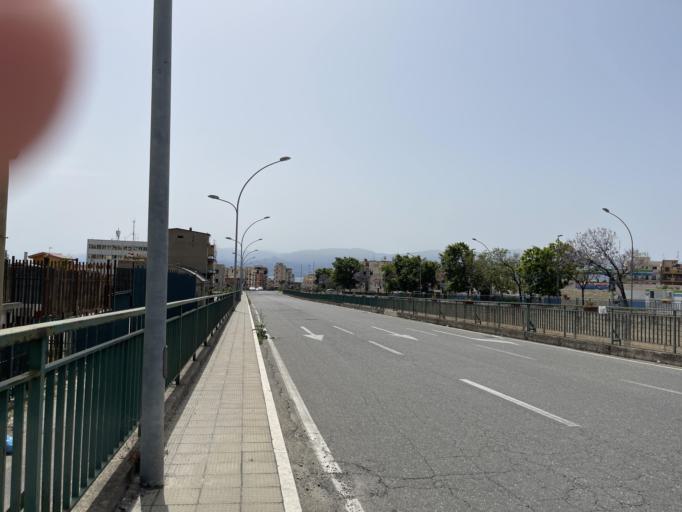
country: IT
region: Calabria
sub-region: Provincia di Reggio Calabria
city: Reggio Calabria
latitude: 38.1012
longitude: 15.6412
